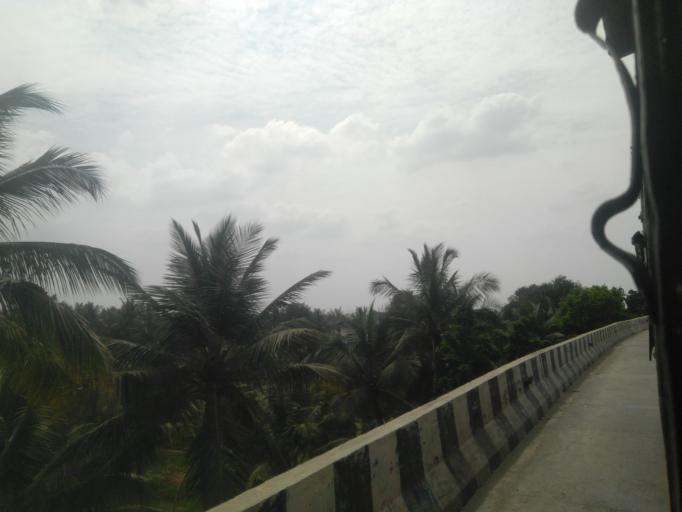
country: IN
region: Tamil Nadu
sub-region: Coimbatore
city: Irugur
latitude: 11.0020
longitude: 77.0562
